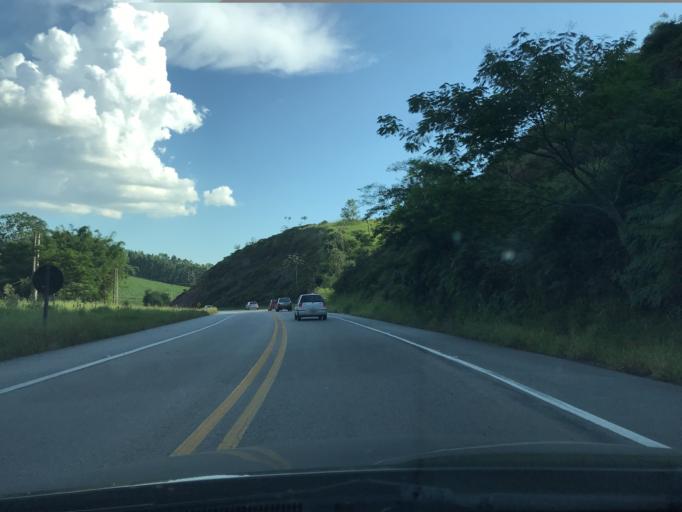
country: BR
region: Sao Paulo
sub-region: Tremembe
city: Tremembe
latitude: -22.8955
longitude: -45.5886
